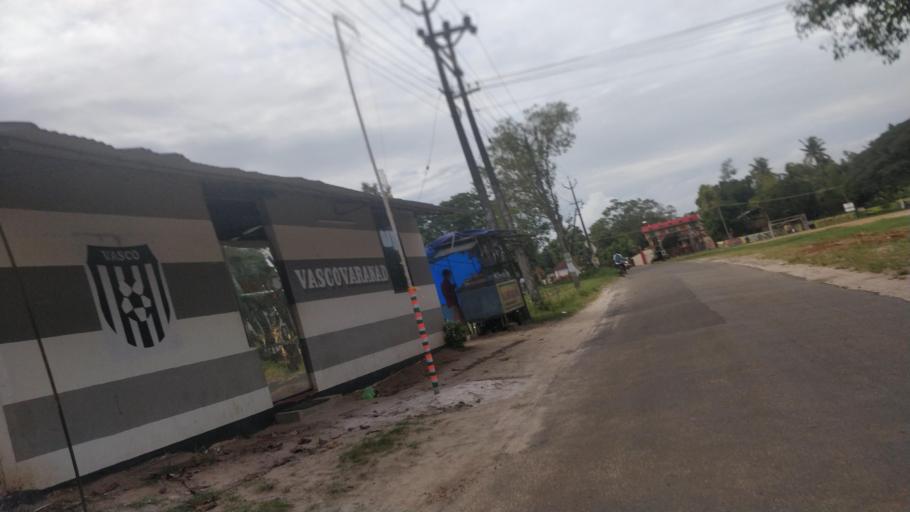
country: IN
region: Kerala
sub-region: Alappuzha
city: Shertallai
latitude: 9.6939
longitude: 76.3612
